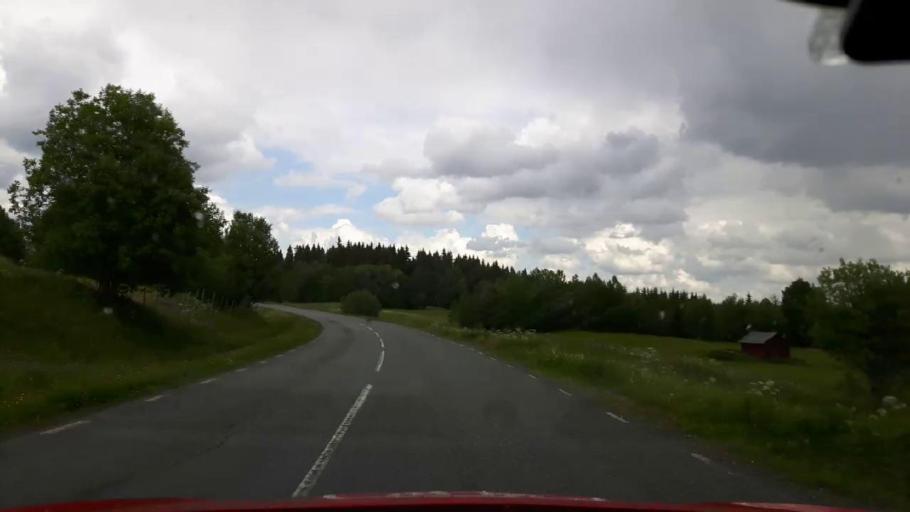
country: SE
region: Jaemtland
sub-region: Krokoms Kommun
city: Krokom
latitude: 63.4941
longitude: 14.2129
